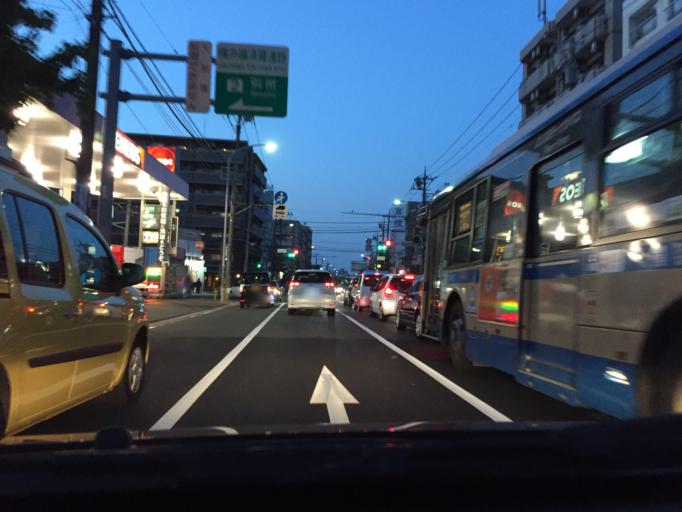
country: JP
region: Kanagawa
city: Yokohama
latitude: 35.4165
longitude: 139.5985
